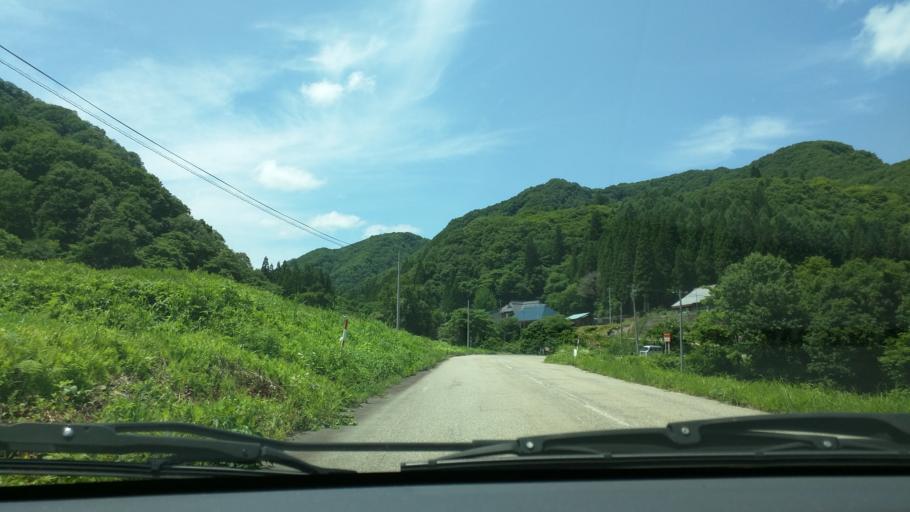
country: JP
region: Fukushima
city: Kitakata
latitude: 37.2573
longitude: 139.7632
